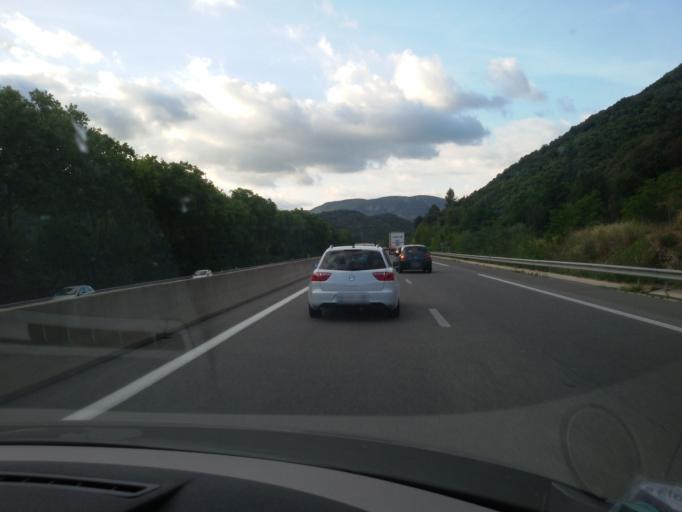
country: FR
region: Languedoc-Roussillon
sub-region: Departement de l'Herault
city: Lodeve
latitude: 43.7059
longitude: 3.3281
